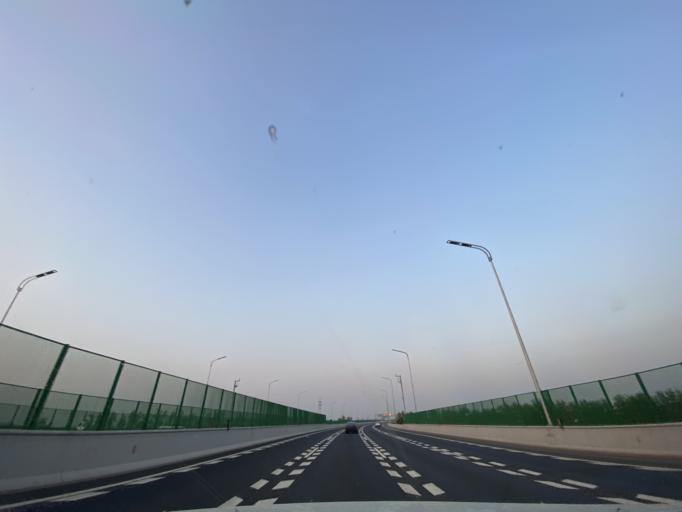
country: CN
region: Beijing
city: Xingfeng
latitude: 39.6907
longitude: 116.3677
